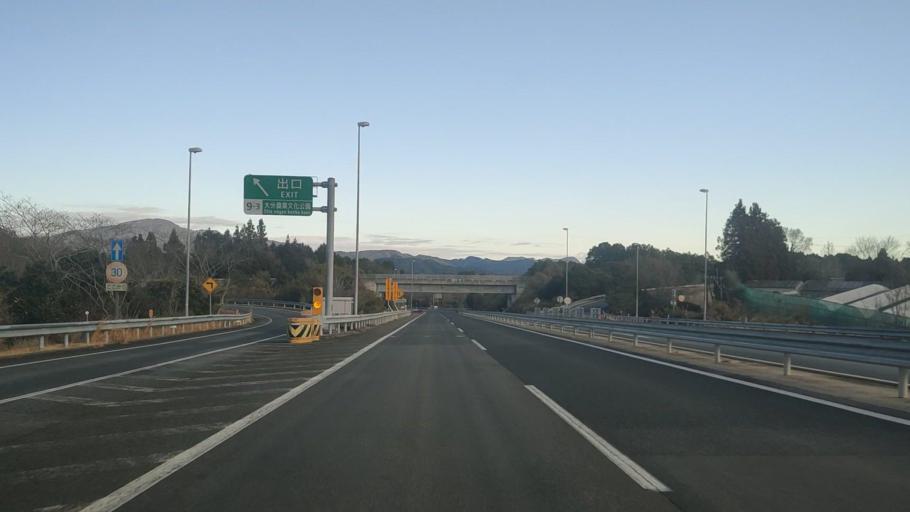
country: JP
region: Oita
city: Hiji
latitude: 33.4213
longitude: 131.4242
